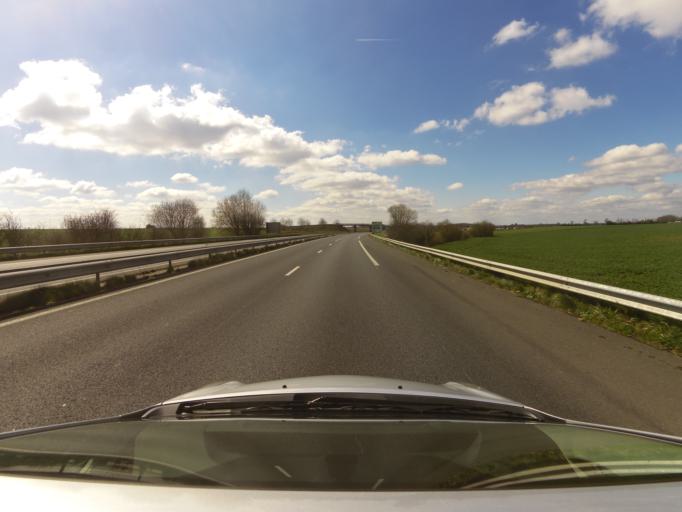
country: FR
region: Haute-Normandie
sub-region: Departement de la Seine-Maritime
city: Saint-Saens
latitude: 49.6819
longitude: 1.3465
